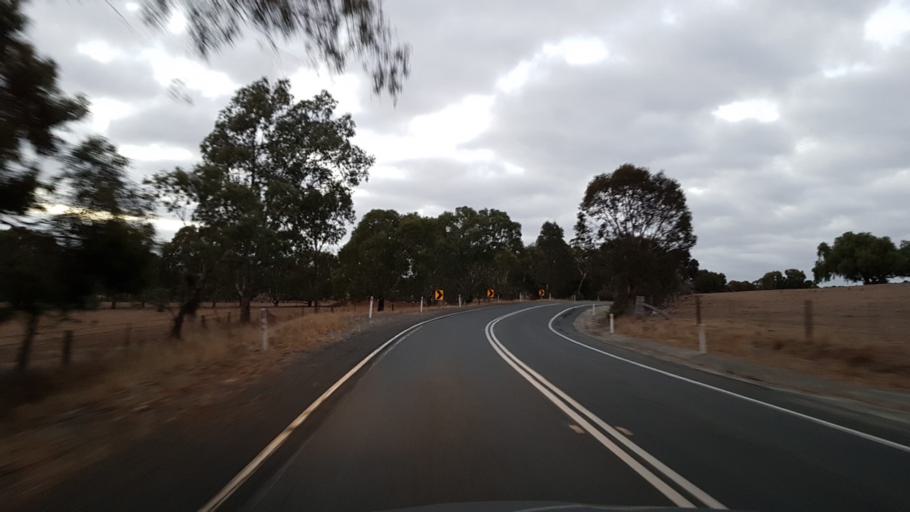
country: AU
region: South Australia
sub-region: Mount Barker
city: Nairne
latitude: -35.0425
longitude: 138.9925
